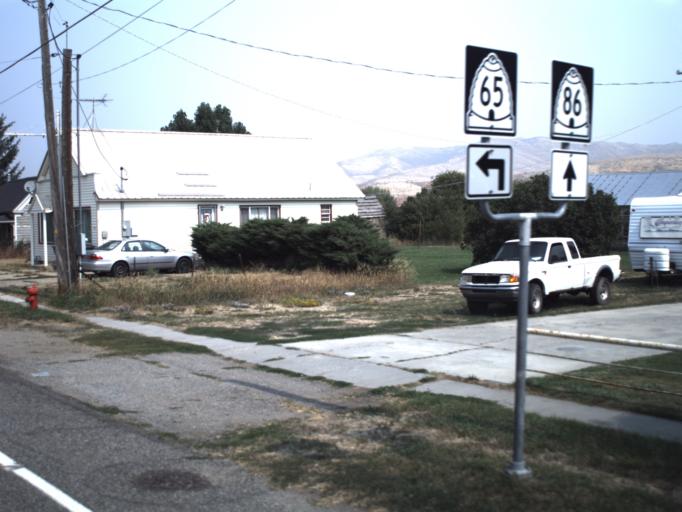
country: US
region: Utah
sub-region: Summit County
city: Coalville
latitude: 41.0202
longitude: -111.5008
